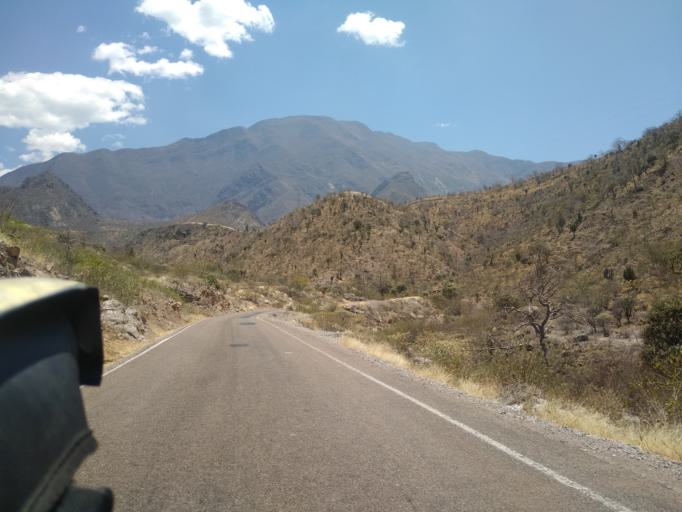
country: PE
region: Amazonas
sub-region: Provincia de Chachapoyas
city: Balsas
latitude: -6.8525
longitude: -78.0336
